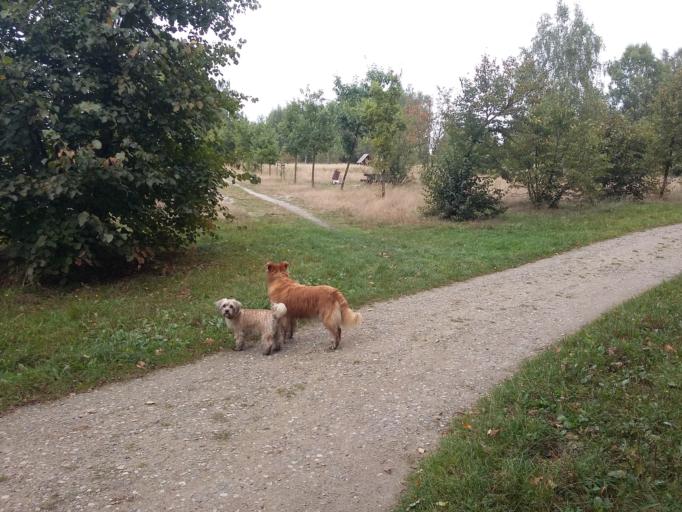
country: PL
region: Lodz Voivodeship
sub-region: Powiat pabianicki
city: Ksawerow
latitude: 51.7287
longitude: 19.3870
